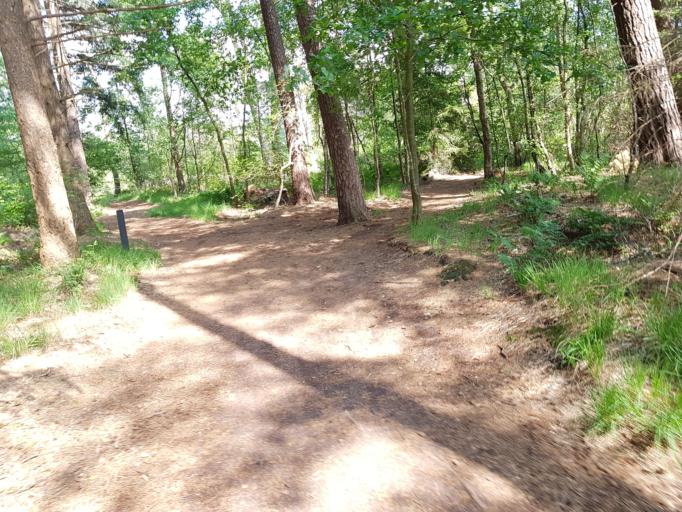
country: NL
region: Friesland
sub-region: Gemeente Heerenveen
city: Jubbega
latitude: 53.0484
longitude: 6.1007
